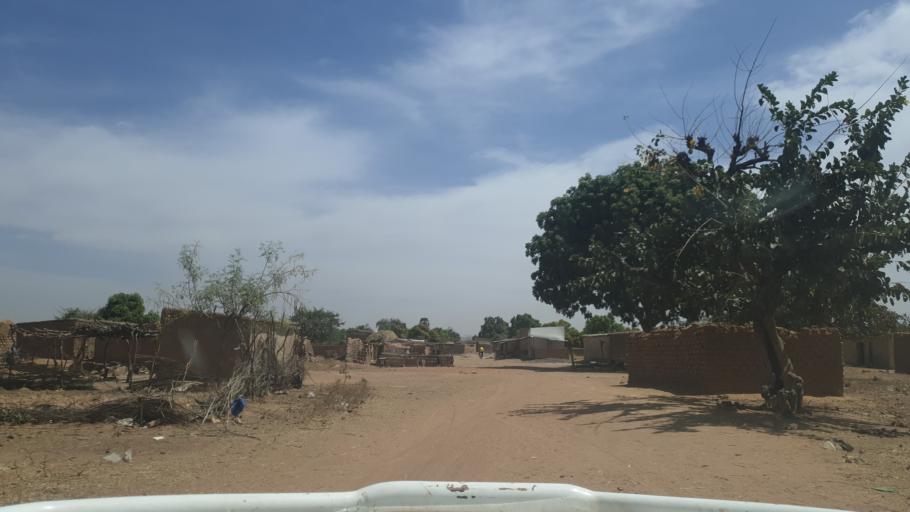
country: ML
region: Sikasso
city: Yorosso
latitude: 12.2913
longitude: -4.6526
